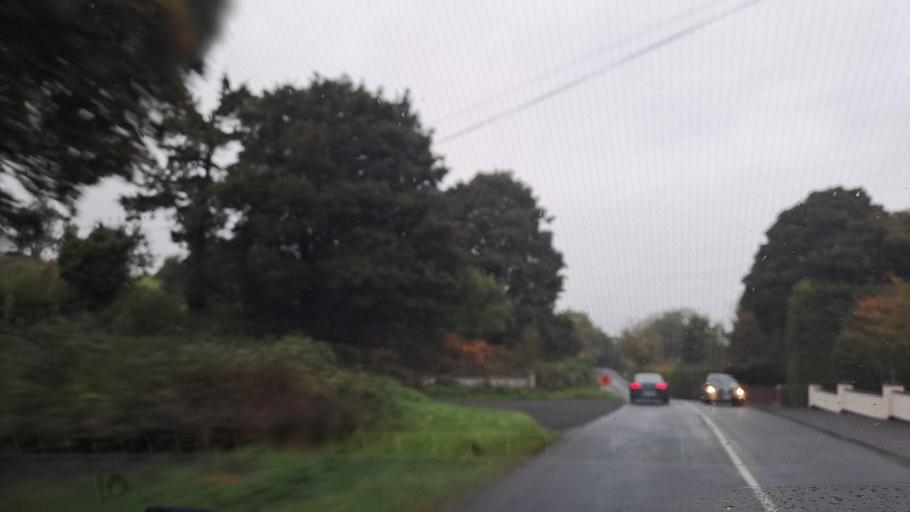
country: IE
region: Ulster
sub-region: County Monaghan
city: Monaghan
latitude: 54.2226
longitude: -6.9285
